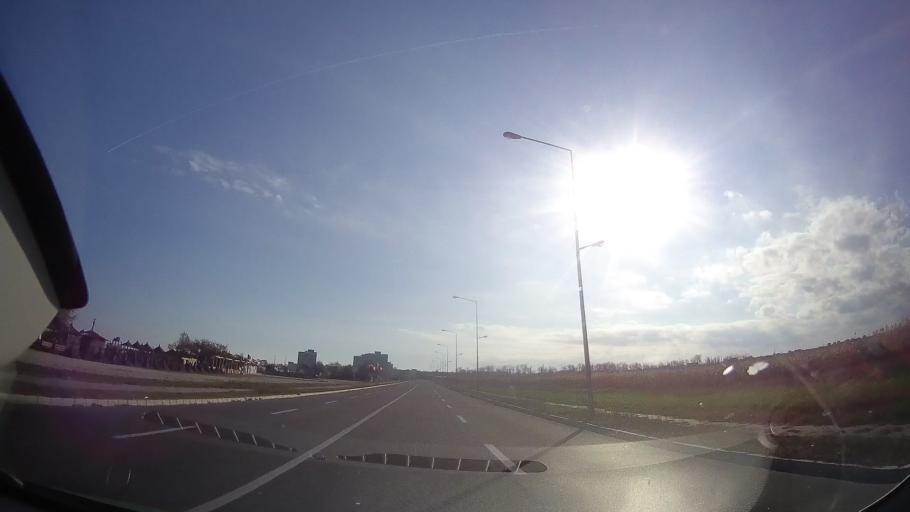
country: RO
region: Constanta
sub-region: Municipiul Mangalia
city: Mangalia
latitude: 43.8393
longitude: 28.5899
